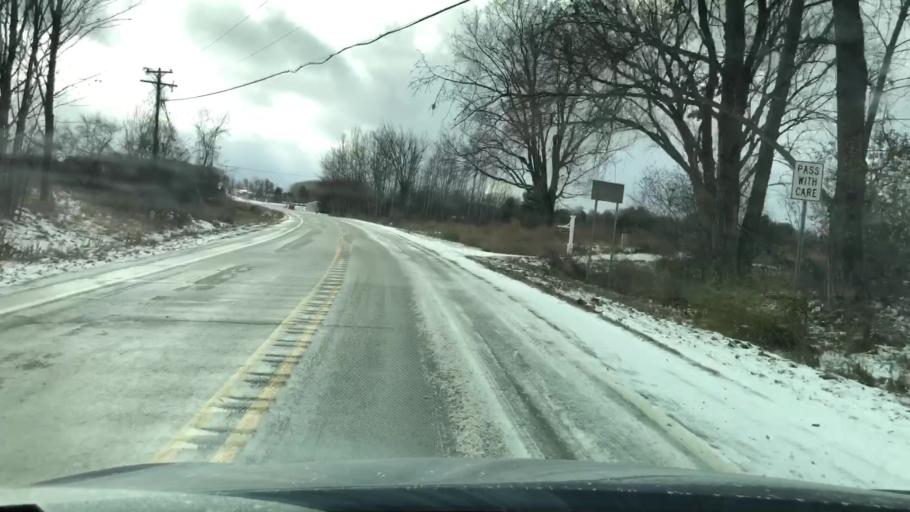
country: US
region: Michigan
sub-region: Antrim County
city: Elk Rapids
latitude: 44.9765
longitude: -85.5045
